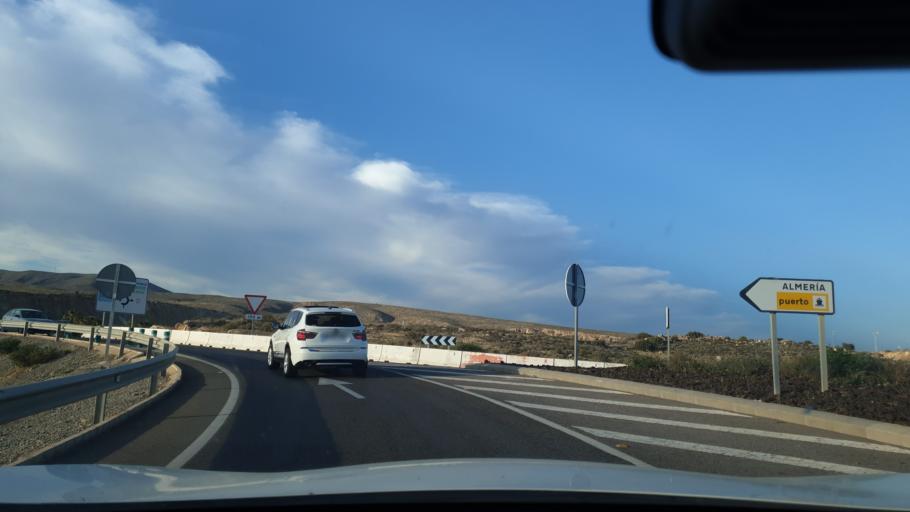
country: ES
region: Andalusia
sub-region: Provincia de Almeria
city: Almeria
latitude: 36.8307
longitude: -2.5031
